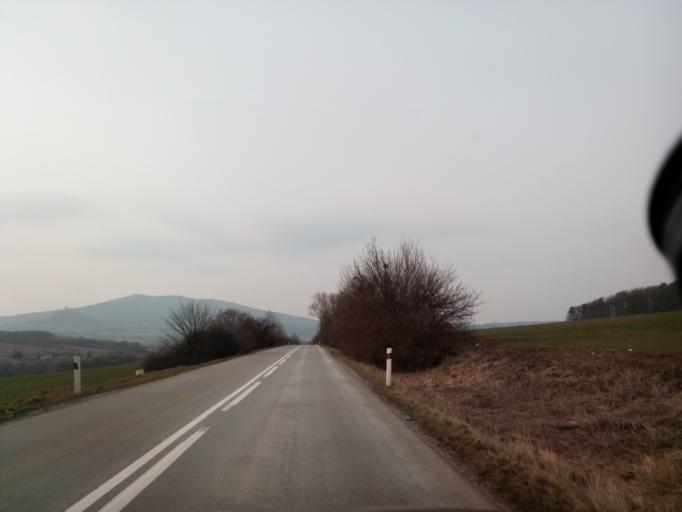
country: SK
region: Kosicky
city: Secovce
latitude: 48.6237
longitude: 21.5344
